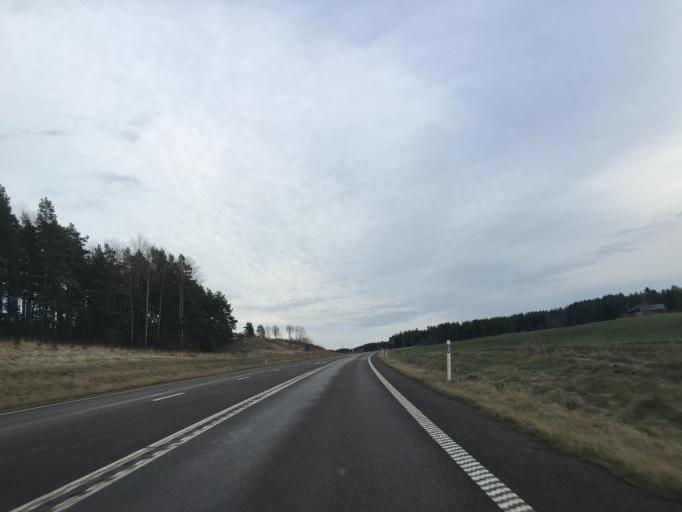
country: SE
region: OEstergoetland
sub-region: Soderkopings Kommun
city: Soederkoeping
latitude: 58.4889
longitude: 16.2509
